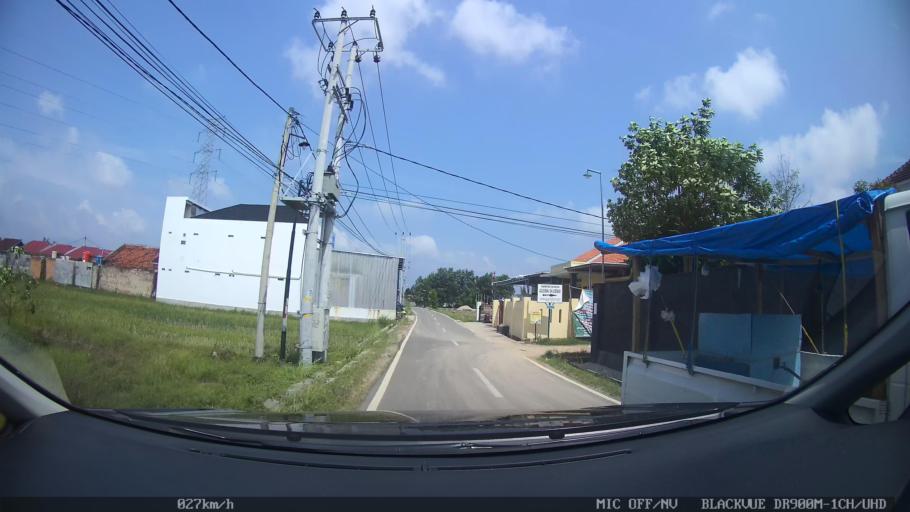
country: ID
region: Lampung
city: Kedaton
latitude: -5.3485
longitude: 105.2794
